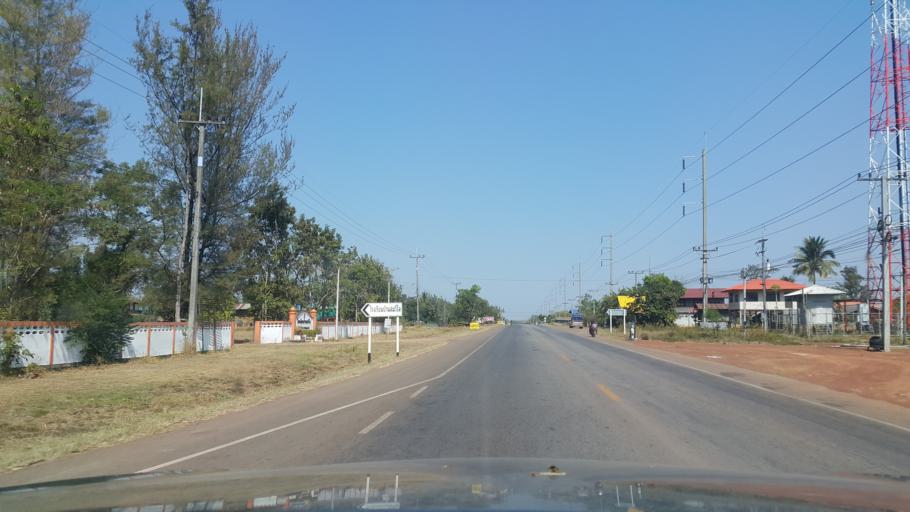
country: TH
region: Changwat Udon Thani
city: Thung Fon
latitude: 17.5628
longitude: 103.2396
